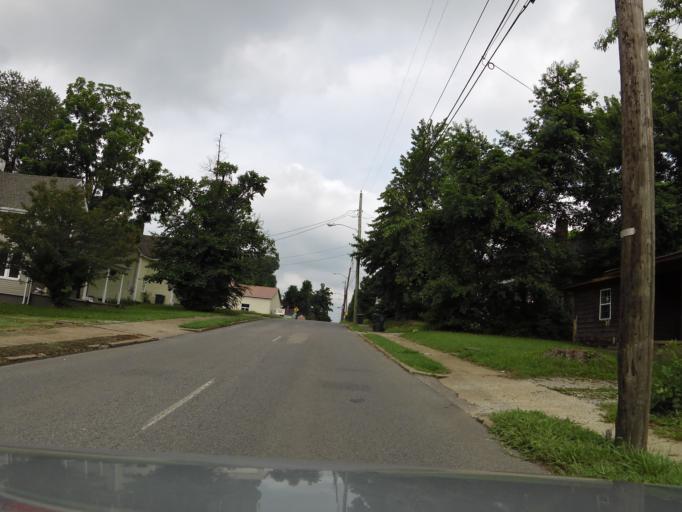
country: US
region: Kentucky
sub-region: Hopkins County
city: Madisonville
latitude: 37.3292
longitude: -87.4904
